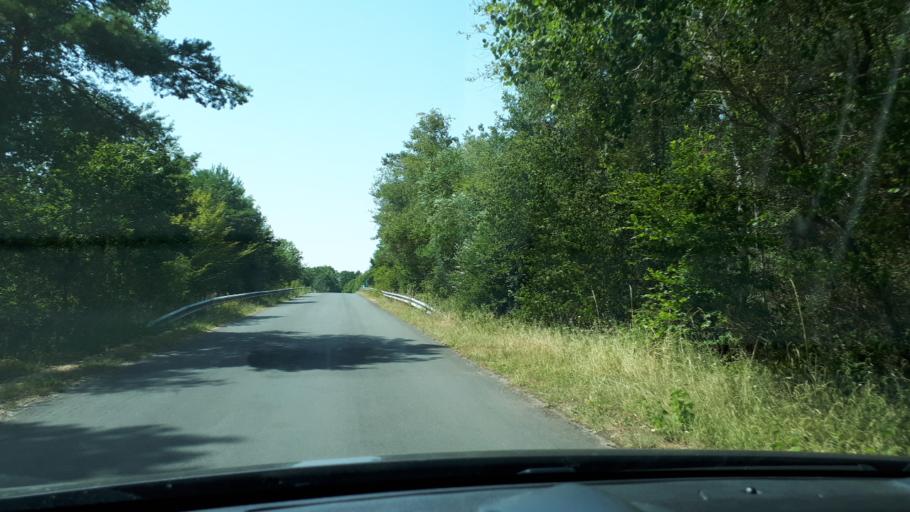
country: FR
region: Centre
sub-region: Departement du Loir-et-Cher
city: Aze
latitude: 47.8368
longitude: 1.0289
